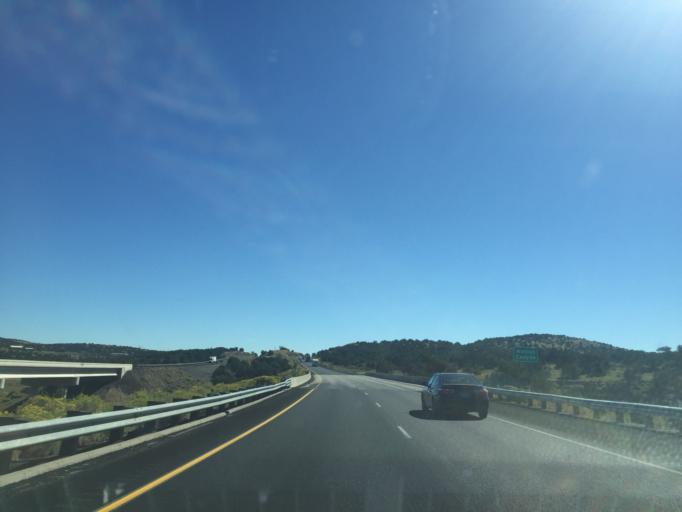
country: US
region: Arizona
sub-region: Coconino County
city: Flagstaff
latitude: 35.2012
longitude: -111.4242
